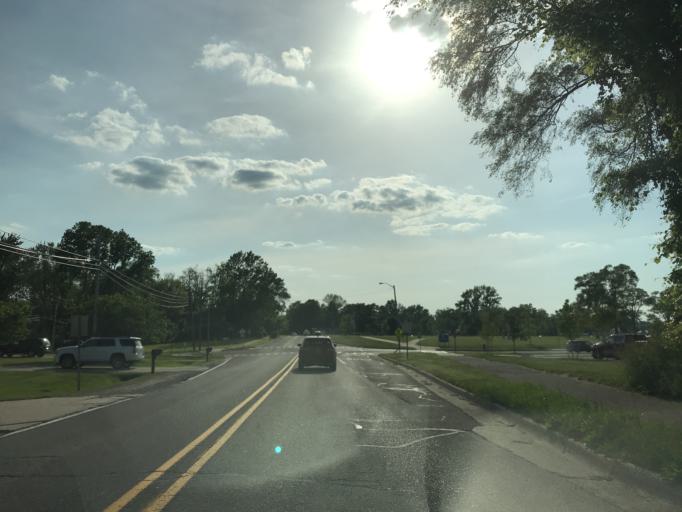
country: US
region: Michigan
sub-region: Oakland County
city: Walled Lake
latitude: 42.5101
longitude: -83.4734
